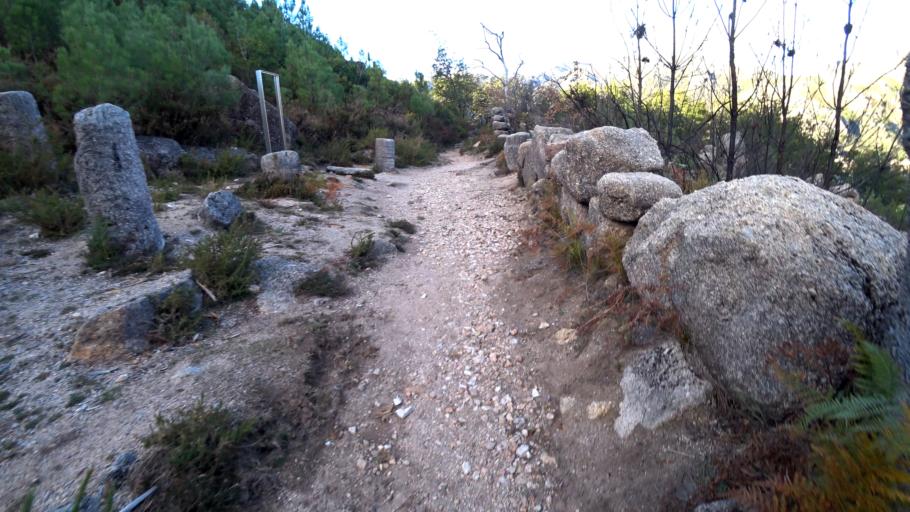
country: PT
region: Braga
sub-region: Terras de Bouro
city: Antas
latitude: 41.7712
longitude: -8.1877
